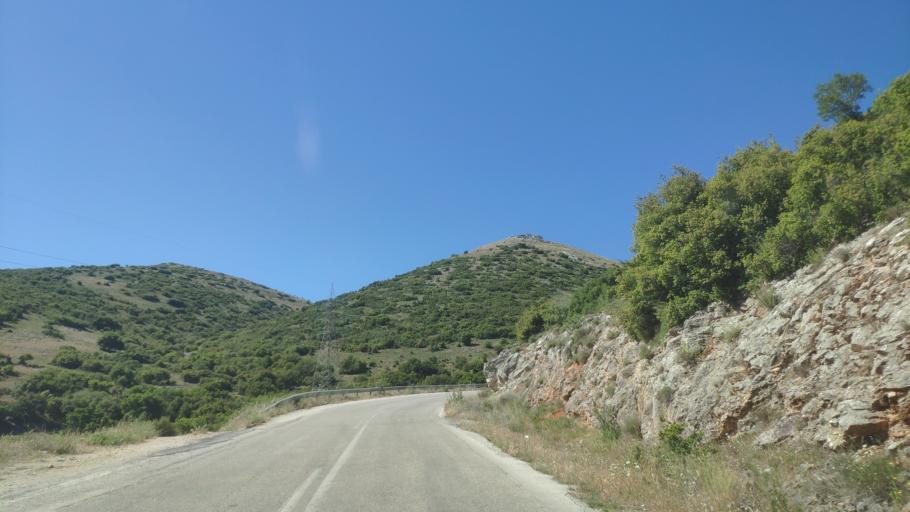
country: GR
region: Peloponnese
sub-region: Nomos Korinthias
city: Khiliomodhi
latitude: 37.7636
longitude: 22.8821
